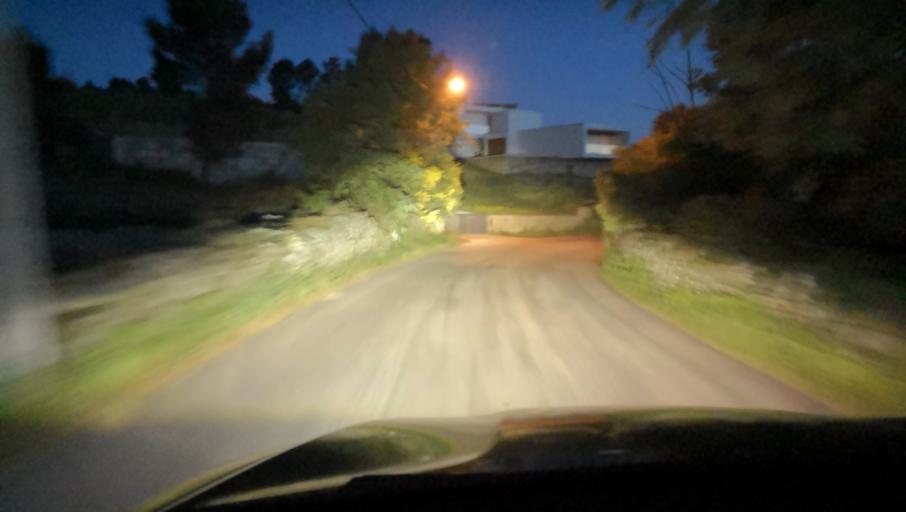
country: PT
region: Vila Real
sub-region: Vila Real
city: Vila Real
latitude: 41.3264
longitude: -7.7053
